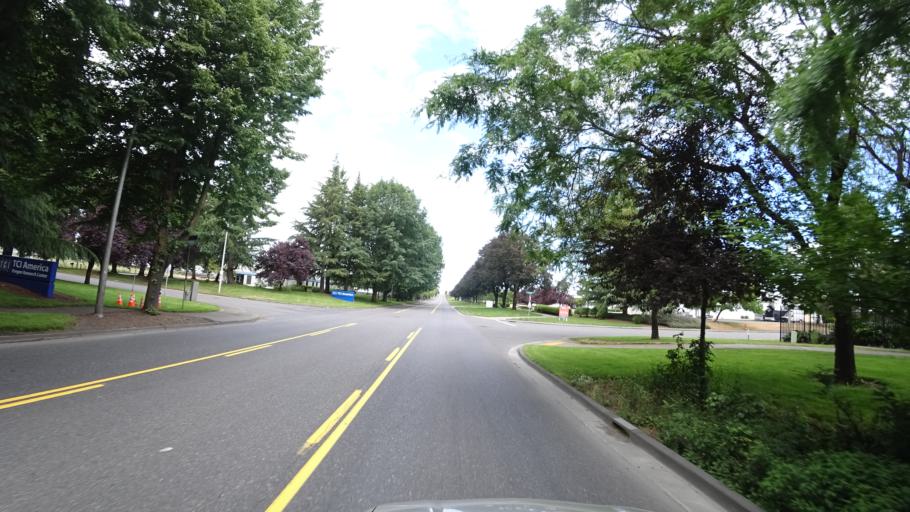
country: US
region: Oregon
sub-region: Washington County
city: West Haven
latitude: 45.6200
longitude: -122.7714
